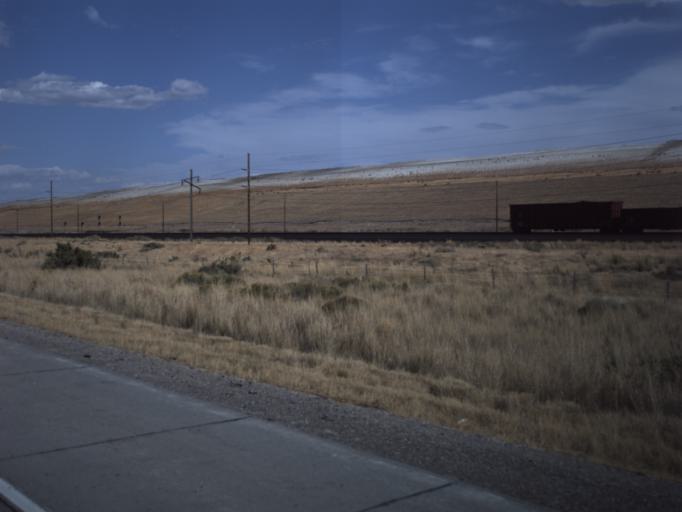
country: US
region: Utah
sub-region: Salt Lake County
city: Magna
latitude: 40.7577
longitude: -112.1679
